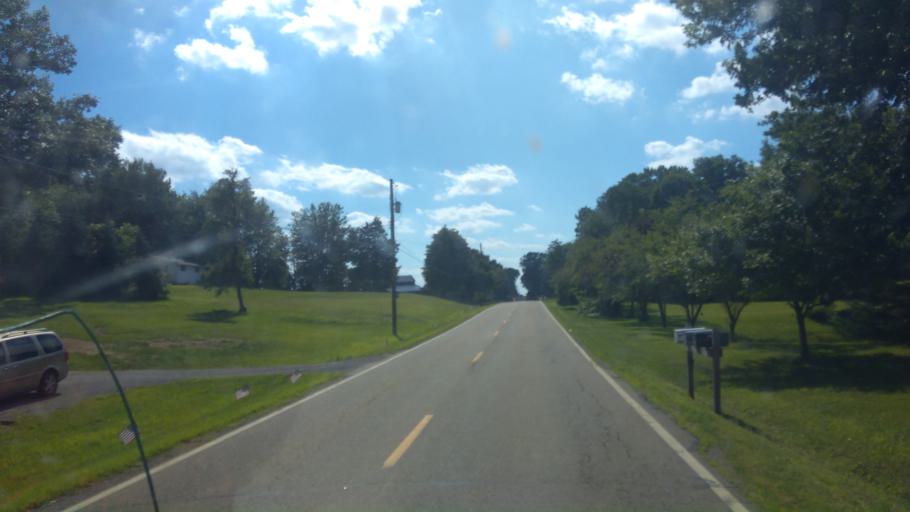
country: US
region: Ohio
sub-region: Stark County
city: Richville
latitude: 40.7307
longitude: -81.4651
